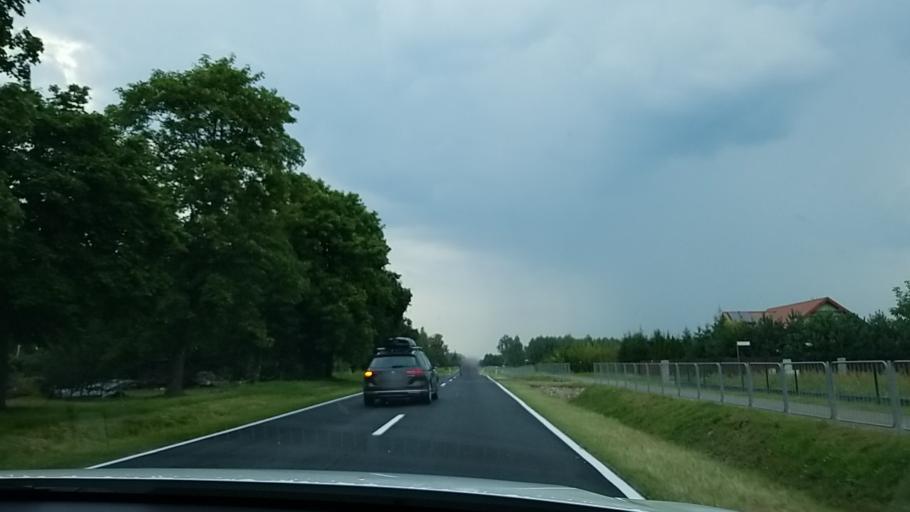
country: PL
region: Lublin Voivodeship
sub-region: Powiat wlodawski
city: Wlodawa
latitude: 51.5702
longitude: 23.5474
